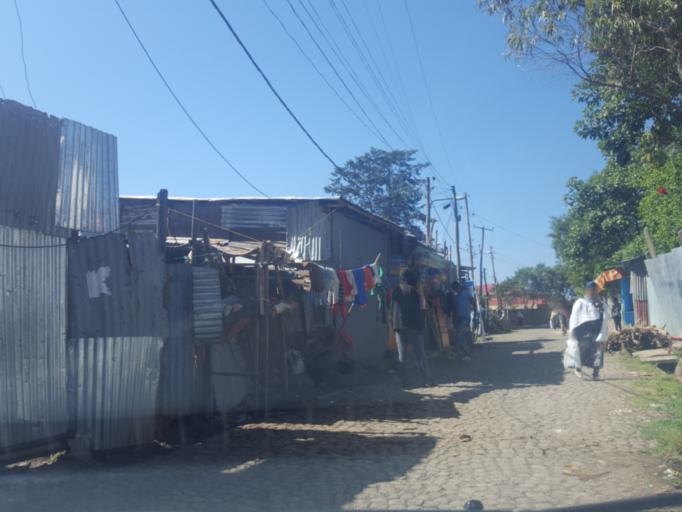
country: ET
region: Adis Abeba
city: Addis Ababa
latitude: 9.0485
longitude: 38.7679
